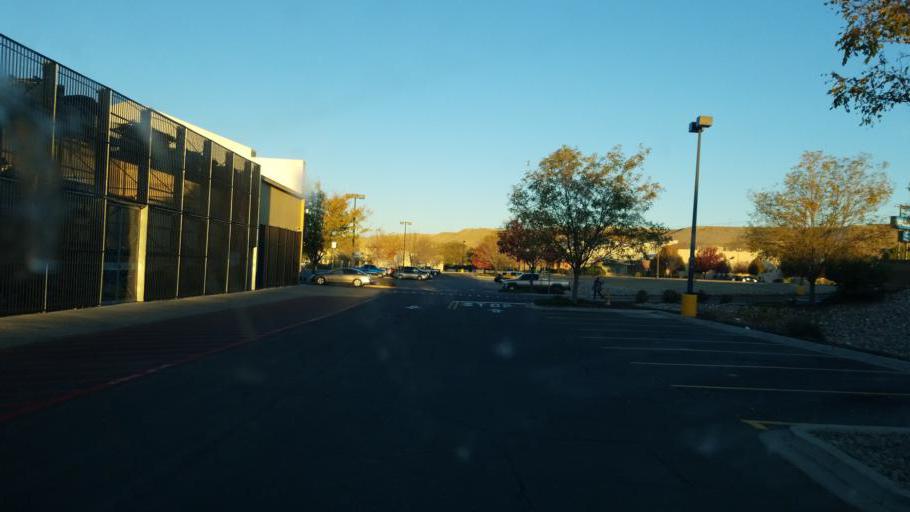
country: US
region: New Mexico
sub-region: San Juan County
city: Farmington
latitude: 36.7329
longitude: -108.2260
